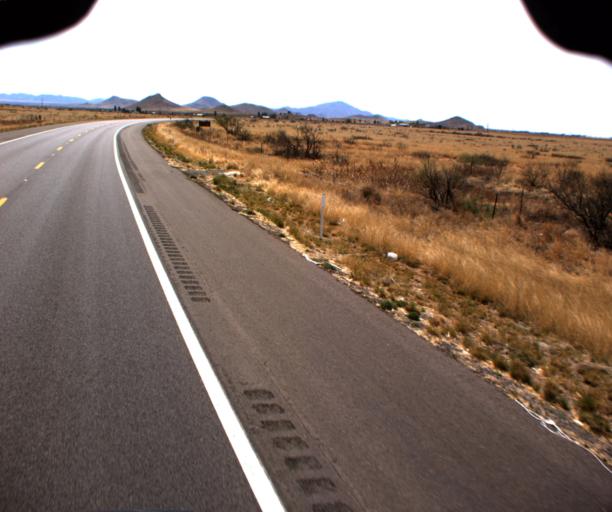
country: US
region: Arizona
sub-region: Cochise County
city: Willcox
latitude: 31.8968
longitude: -109.7005
